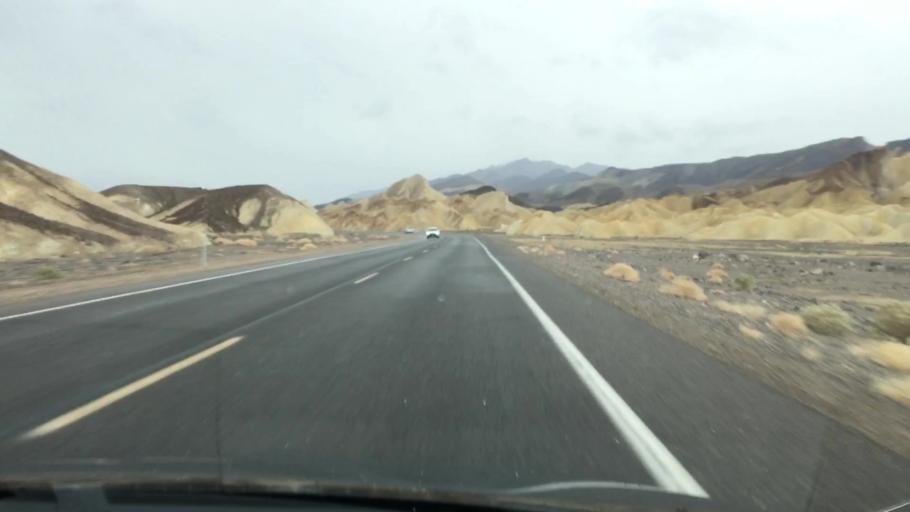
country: US
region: Nevada
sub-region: Nye County
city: Beatty
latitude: 36.4167
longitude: -116.8049
